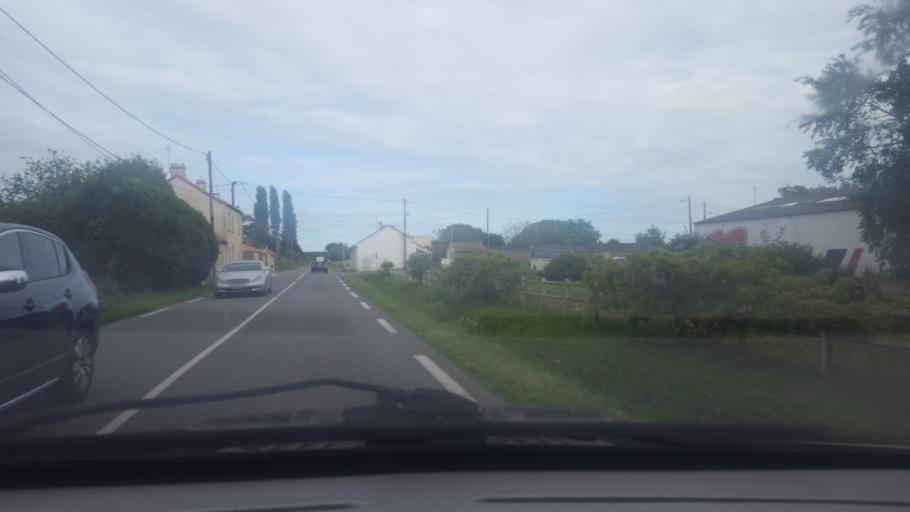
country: FR
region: Pays de la Loire
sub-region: Departement de la Loire-Atlantique
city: Machecoul
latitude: 47.0214
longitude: -1.8715
